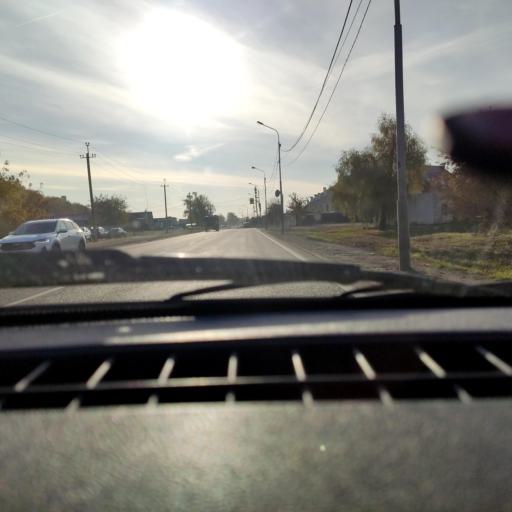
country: RU
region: Bashkortostan
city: Ufa
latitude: 54.6944
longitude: 55.9770
